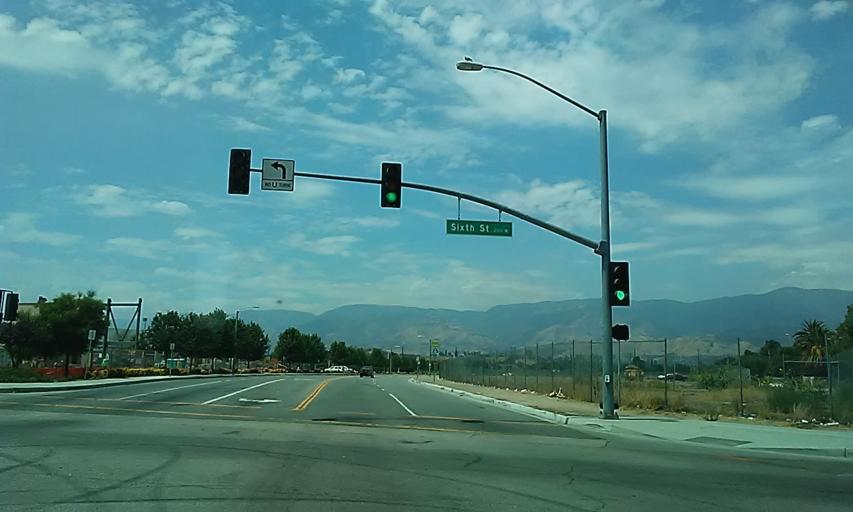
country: US
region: California
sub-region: San Bernardino County
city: San Bernardino
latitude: 34.1101
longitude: -117.2517
